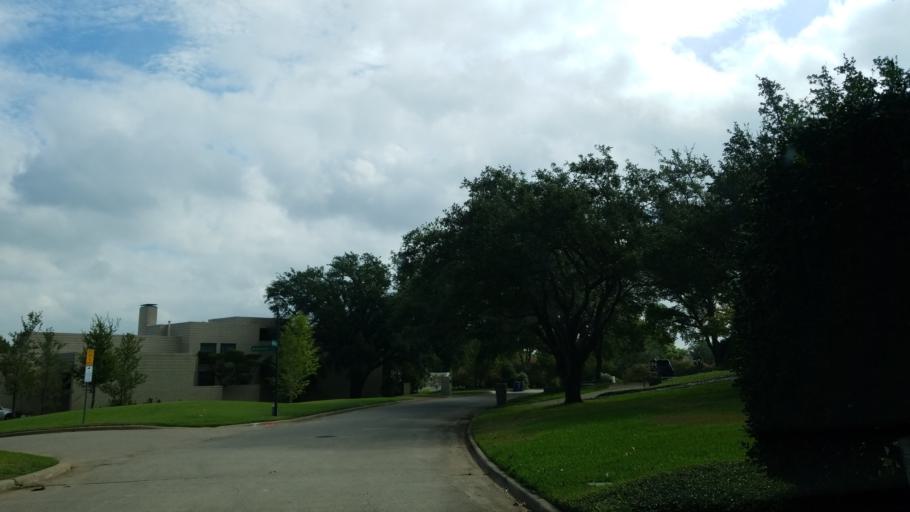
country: US
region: Texas
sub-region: Dallas County
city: Addison
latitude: 32.9437
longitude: -96.8002
